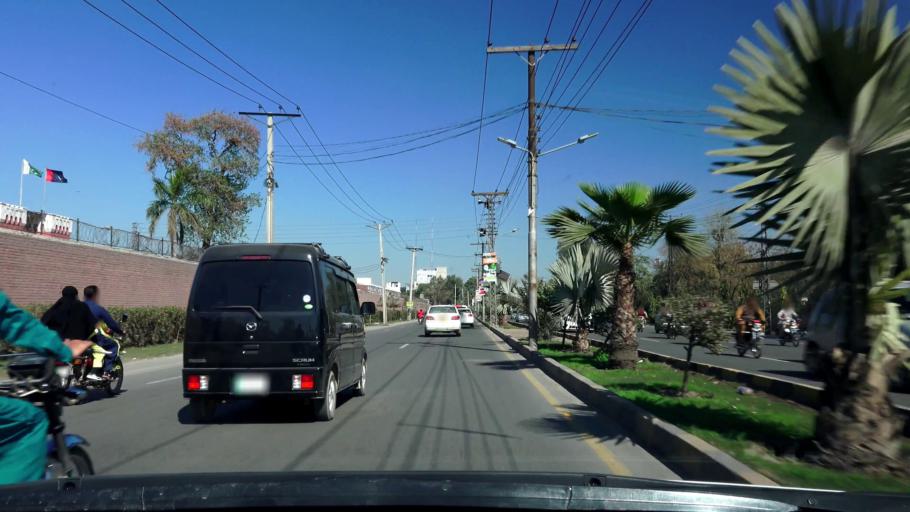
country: PK
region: Punjab
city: Faisalabad
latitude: 31.4305
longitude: 73.0773
